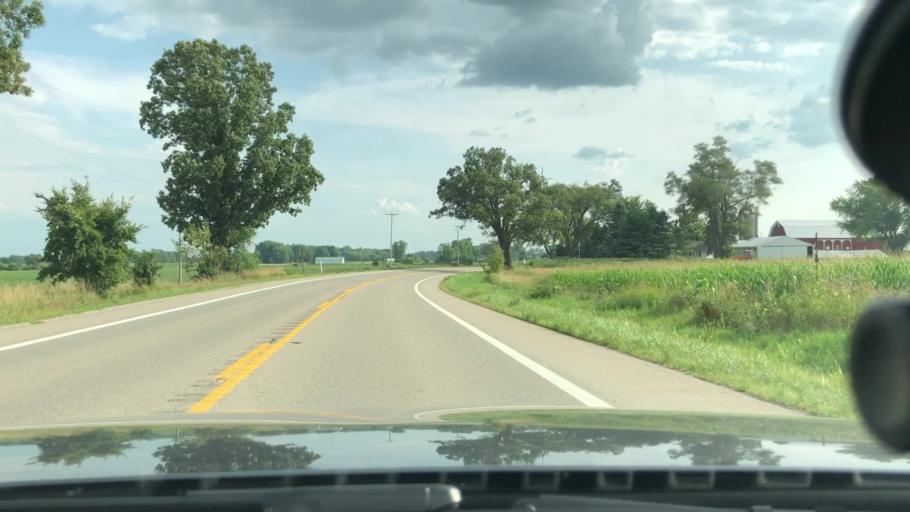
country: US
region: Michigan
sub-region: Washtenaw County
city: Chelsea
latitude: 42.2773
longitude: -84.0316
